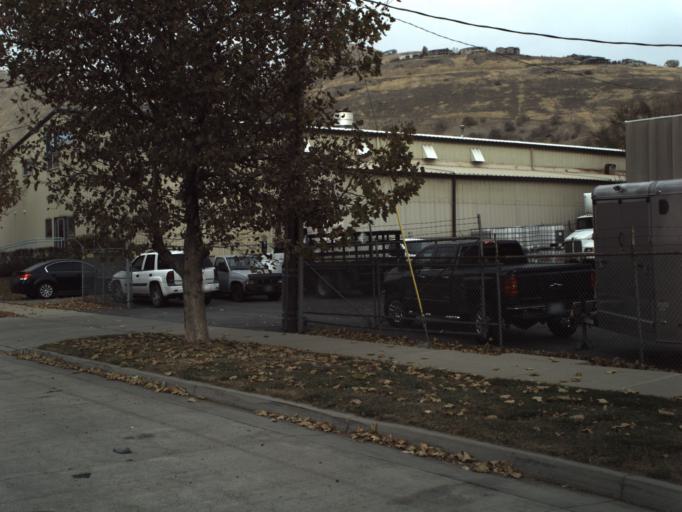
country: US
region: Utah
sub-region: Salt Lake County
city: Salt Lake City
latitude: 40.7827
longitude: -111.9024
